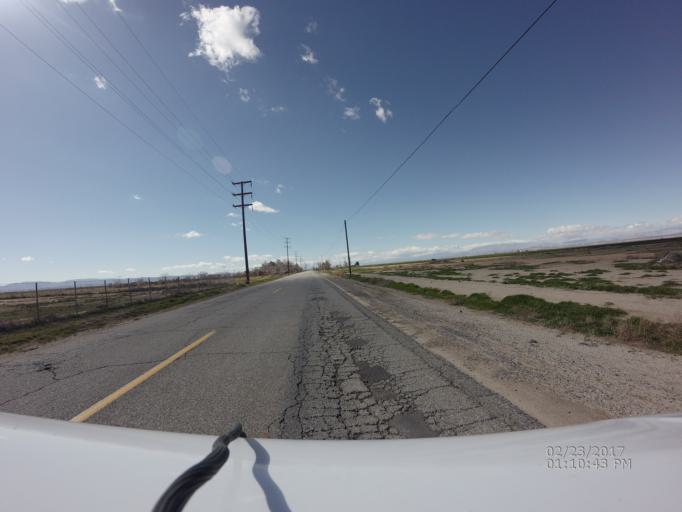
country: US
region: California
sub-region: Los Angeles County
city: Lancaster
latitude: 34.7633
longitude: -118.0158
